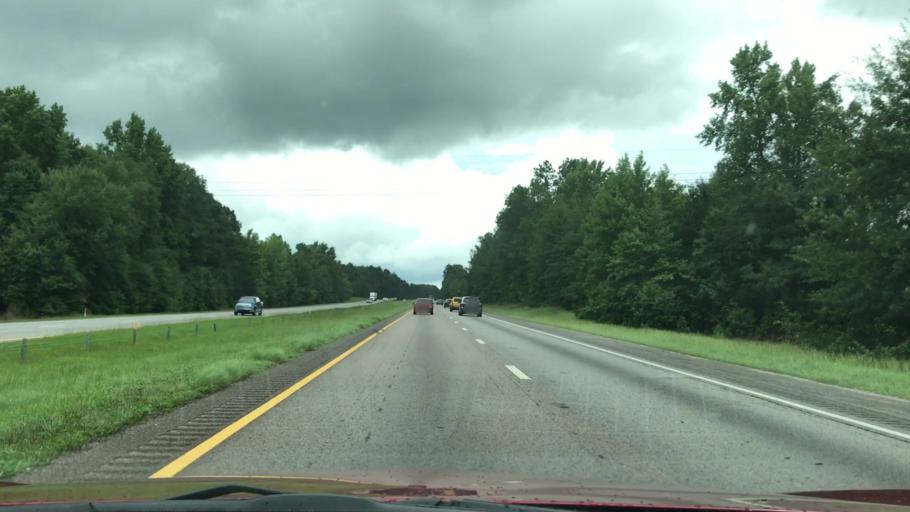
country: US
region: South Carolina
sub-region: Calhoun County
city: Saint Matthews
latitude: 33.6600
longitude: -80.8893
